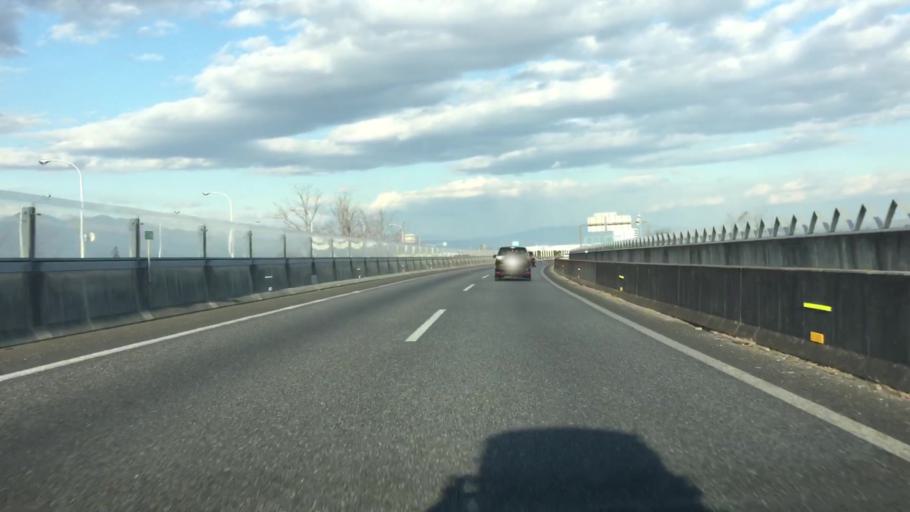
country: JP
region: Gunma
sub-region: Sawa-gun
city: Tamamura
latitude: 36.3303
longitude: 139.0803
